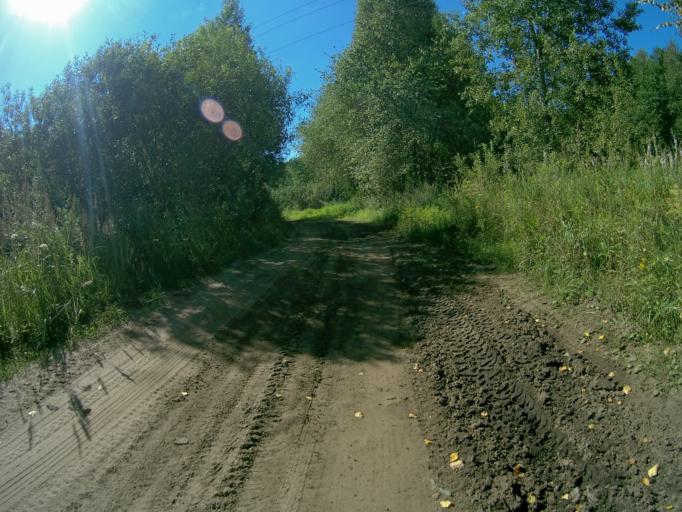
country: RU
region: Vladimir
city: Raduzhnyy
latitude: 55.9402
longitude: 40.2410
